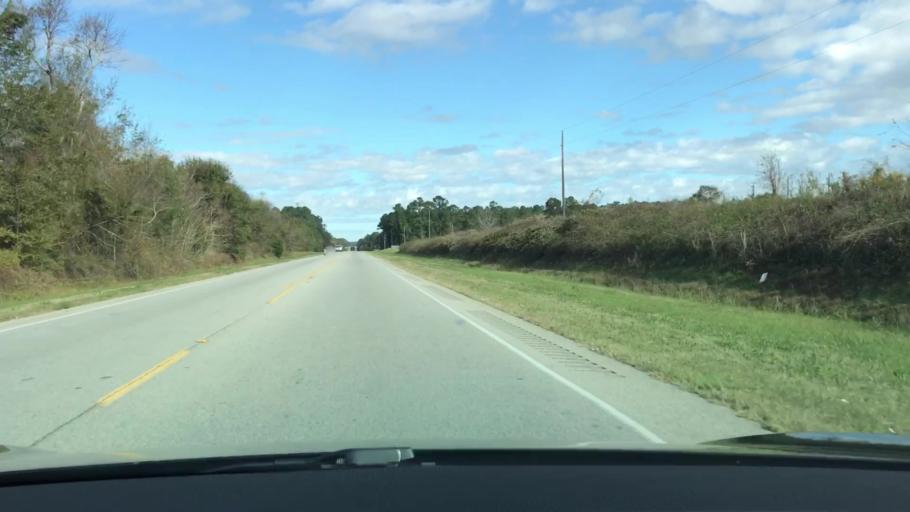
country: US
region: Georgia
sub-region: Jefferson County
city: Wadley
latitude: 32.9306
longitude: -82.3968
